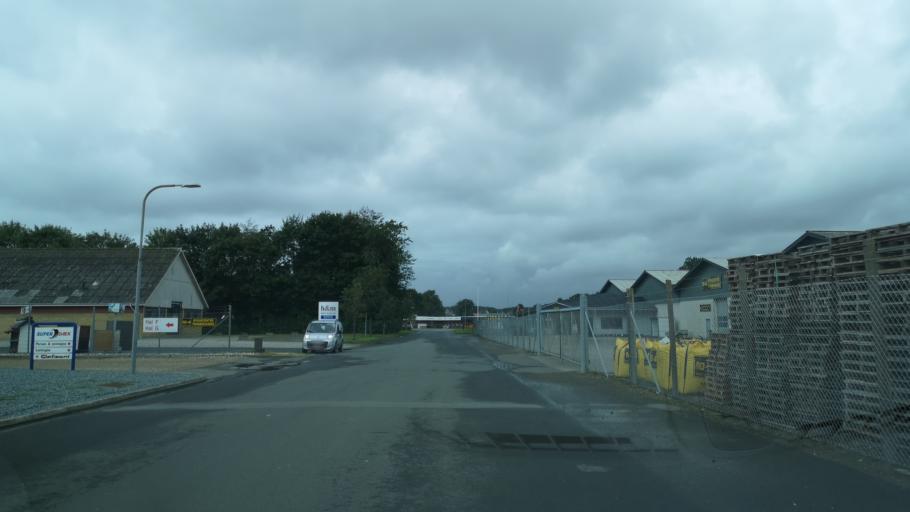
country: DK
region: Central Jutland
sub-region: Ringkobing-Skjern Kommune
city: Videbaek
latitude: 56.0903
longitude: 8.6418
